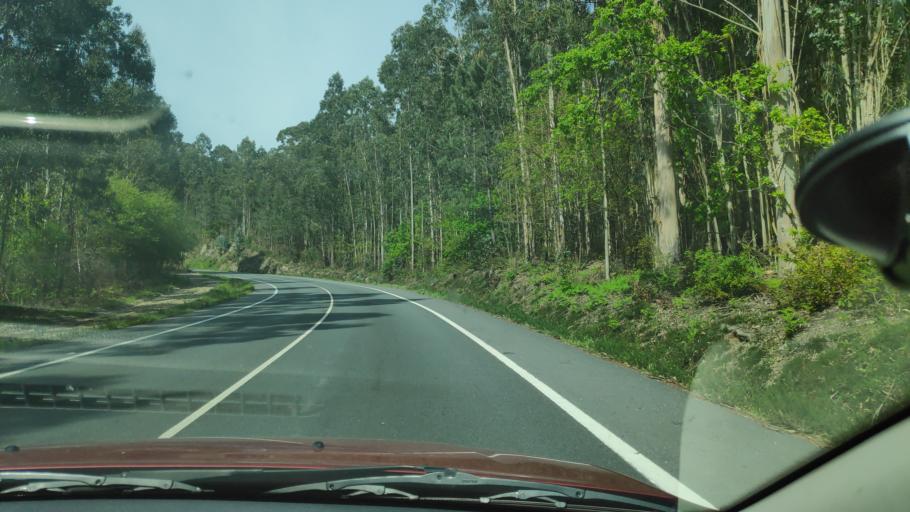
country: ES
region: Galicia
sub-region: Provincia da Coruna
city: Ames
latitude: 42.8738
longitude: -8.6589
